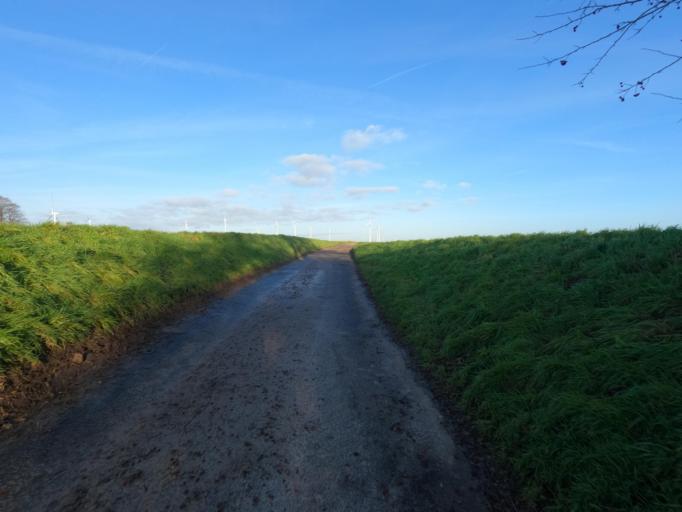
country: DE
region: North Rhine-Westphalia
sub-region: Regierungsbezirk Koln
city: Elsdorf
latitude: 50.9623
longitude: 6.5013
